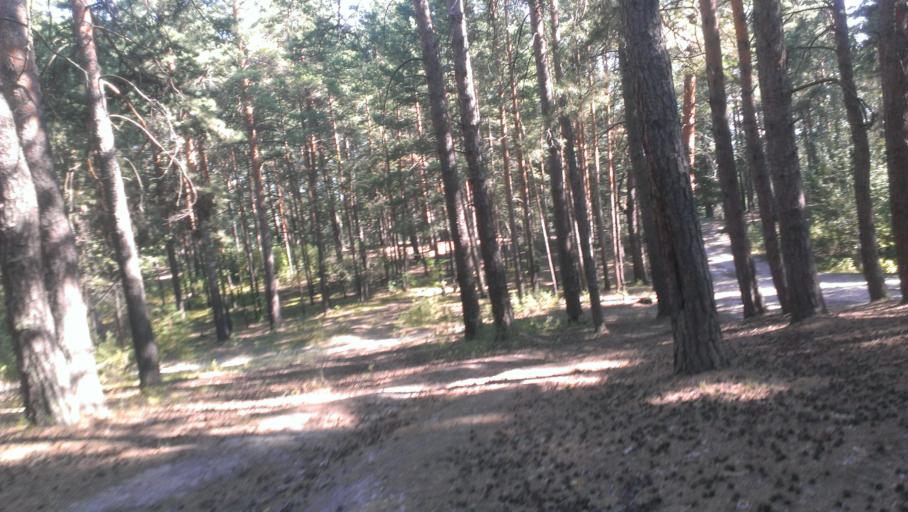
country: RU
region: Altai Krai
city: Yuzhnyy
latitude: 53.3163
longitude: 83.6886
